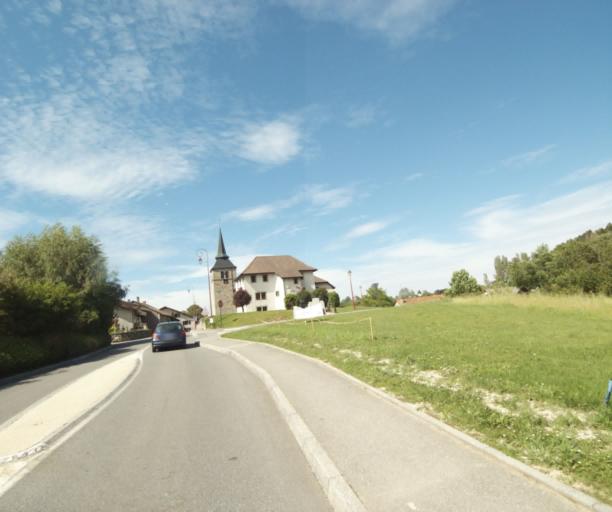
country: FR
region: Rhone-Alpes
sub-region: Departement de la Haute-Savoie
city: Perrignier
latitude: 46.3022
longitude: 6.4574
